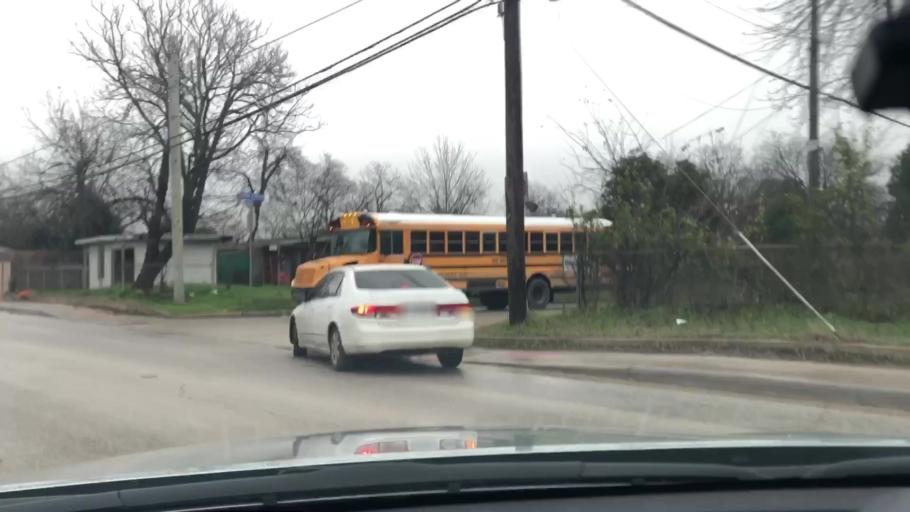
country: US
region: Texas
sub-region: Bexar County
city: Kirby
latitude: 29.4356
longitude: -98.4109
